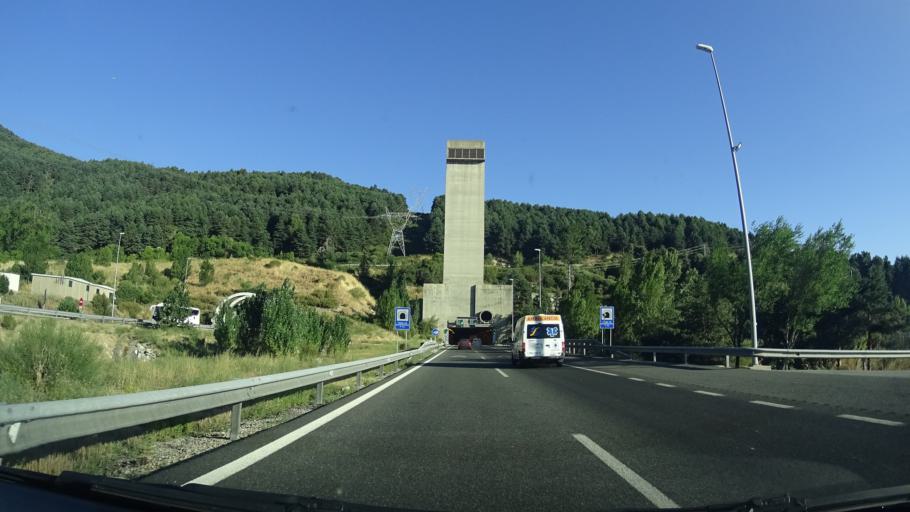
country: ES
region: Madrid
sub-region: Provincia de Madrid
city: Guadarrama
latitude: 40.6991
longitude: -4.1285
